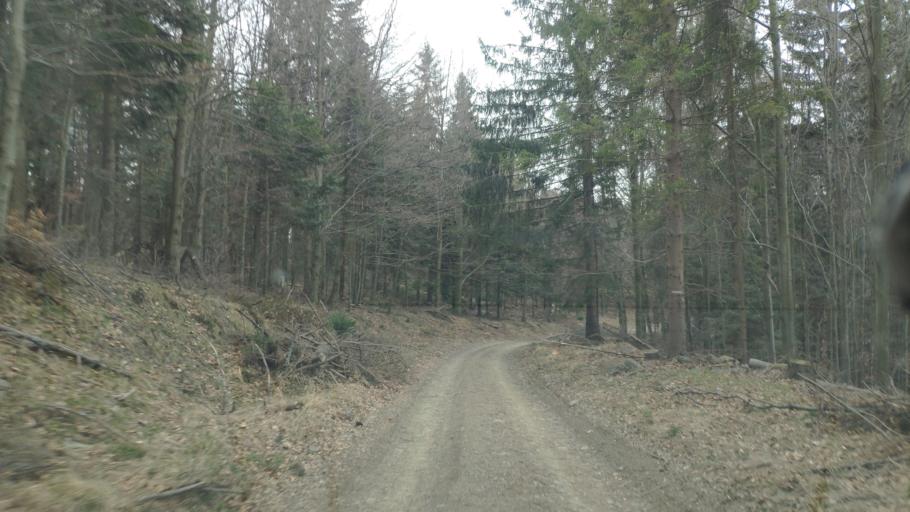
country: SK
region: Kosicky
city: Moldava nad Bodvou
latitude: 48.7529
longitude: 21.0416
